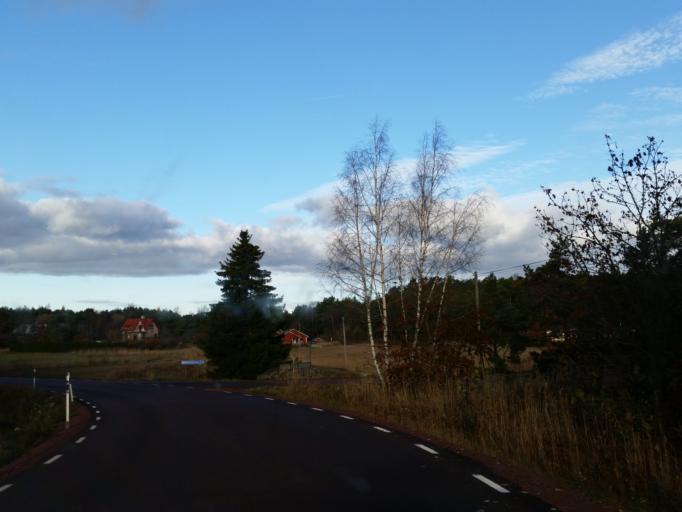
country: AX
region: Alands skaergard
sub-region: Foegloe
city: Foegloe
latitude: 60.0379
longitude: 20.5393
